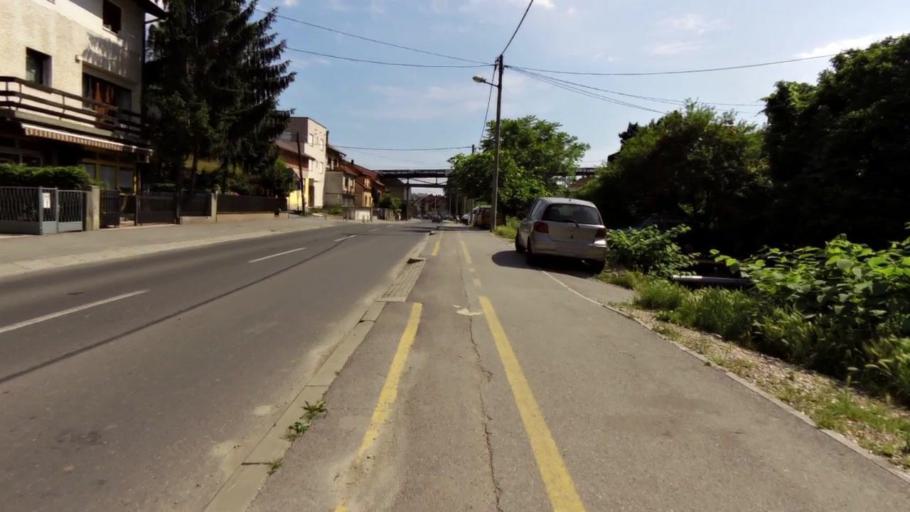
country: HR
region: Grad Zagreb
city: Jankomir
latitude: 45.8173
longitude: 15.9266
